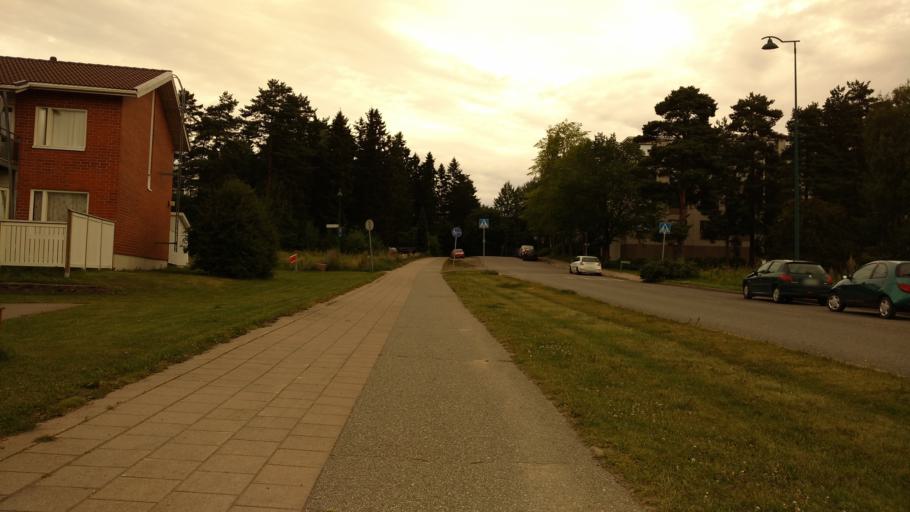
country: FI
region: Varsinais-Suomi
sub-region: Turku
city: Kaarina
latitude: 60.4404
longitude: 22.3635
